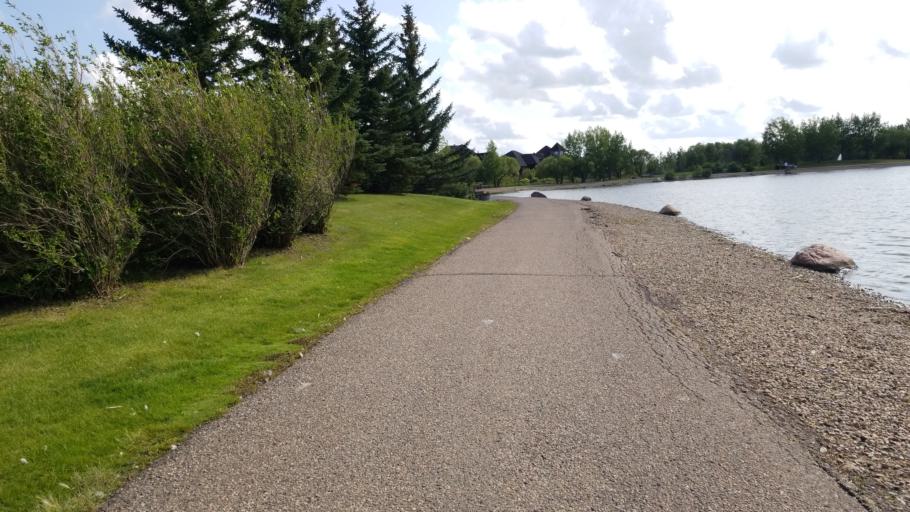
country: CA
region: Saskatchewan
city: Lloydminster
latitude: 53.2595
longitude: -110.0392
